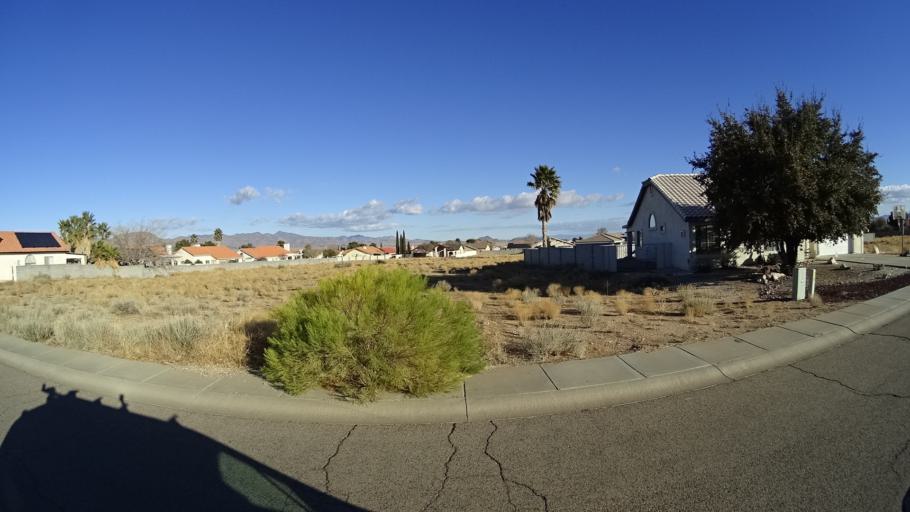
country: US
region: Arizona
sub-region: Mohave County
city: New Kingman-Butler
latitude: 35.2210
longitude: -113.9742
